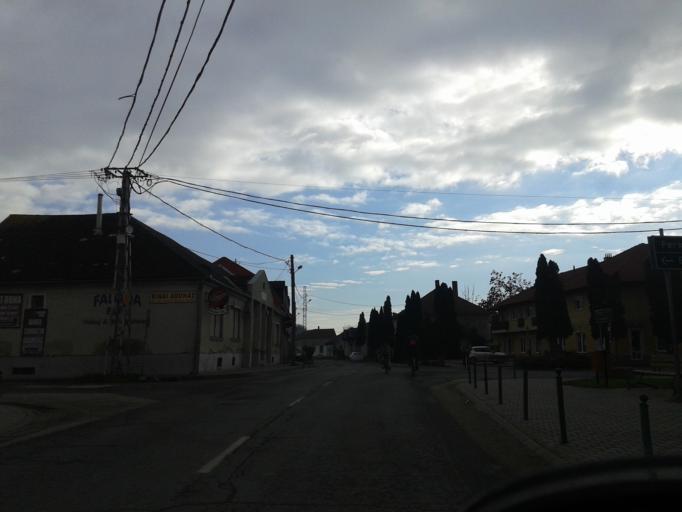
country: HU
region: Fejer
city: Adony
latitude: 47.1196
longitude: 18.8651
